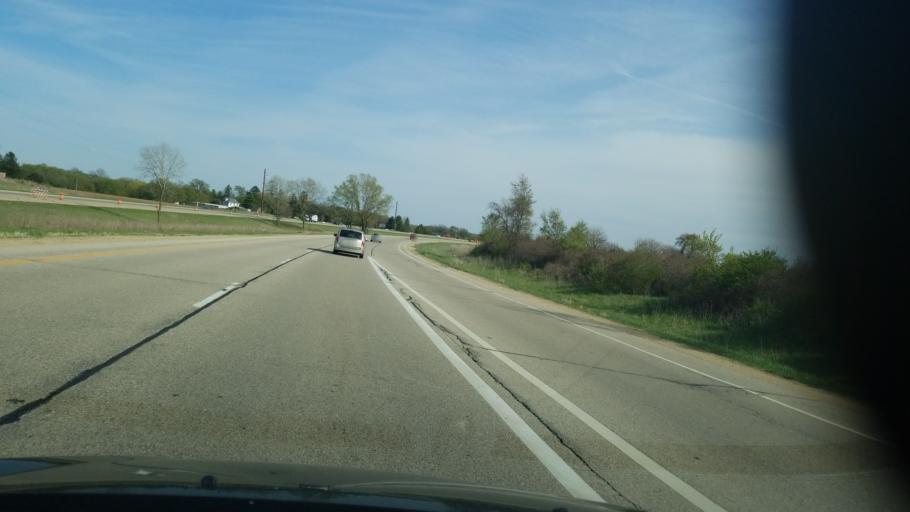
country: US
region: Wisconsin
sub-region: Dane County
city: Oregon
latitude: 42.9494
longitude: -89.3738
